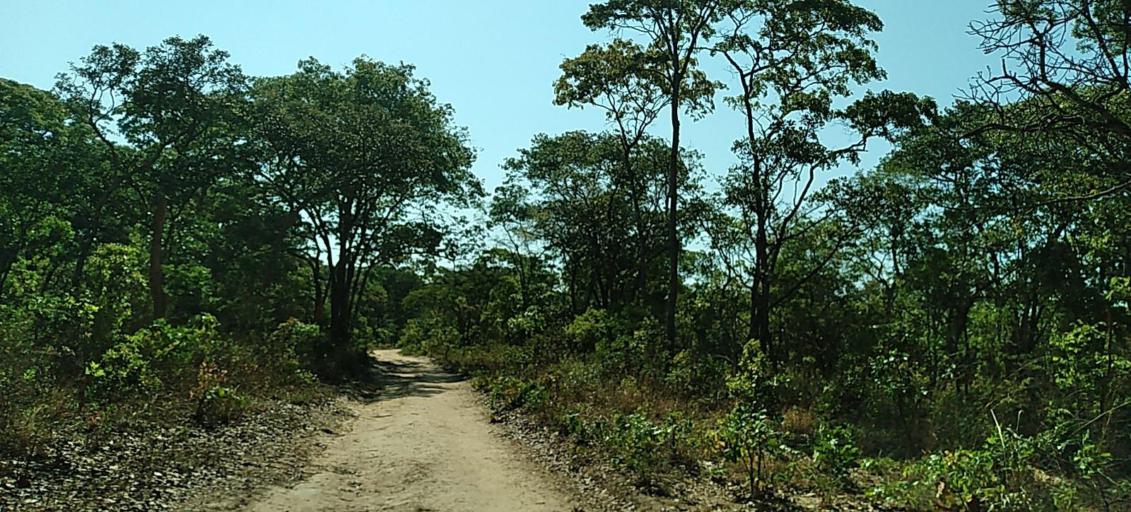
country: ZM
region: Central
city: Mkushi
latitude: -13.4711
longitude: 28.9782
